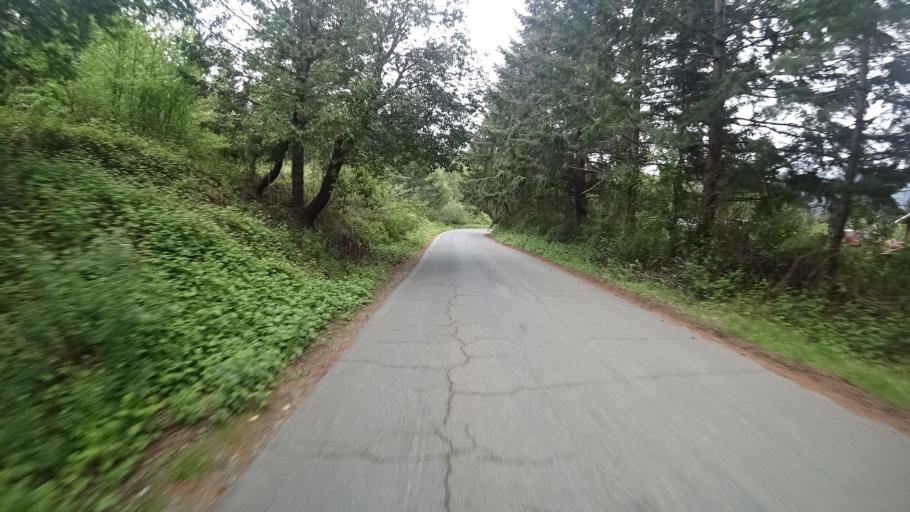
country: US
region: California
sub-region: Humboldt County
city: Willow Creek
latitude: 41.1139
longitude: -123.7163
